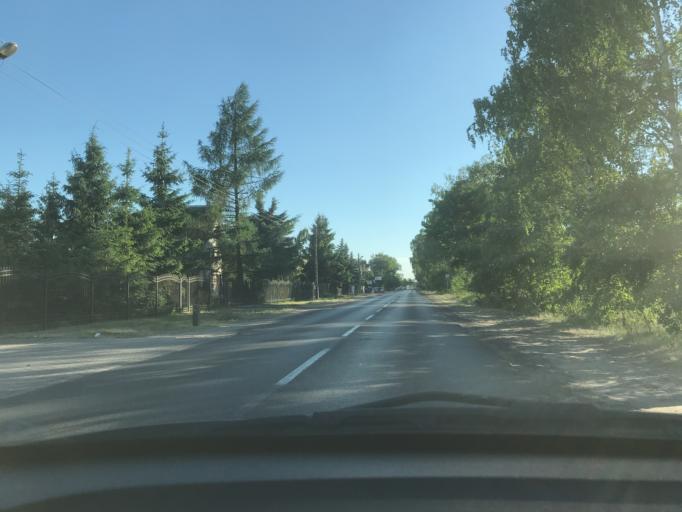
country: PL
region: Greater Poland Voivodeship
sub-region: Powiat poznanski
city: Plewiska
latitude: 52.4004
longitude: 16.8081
